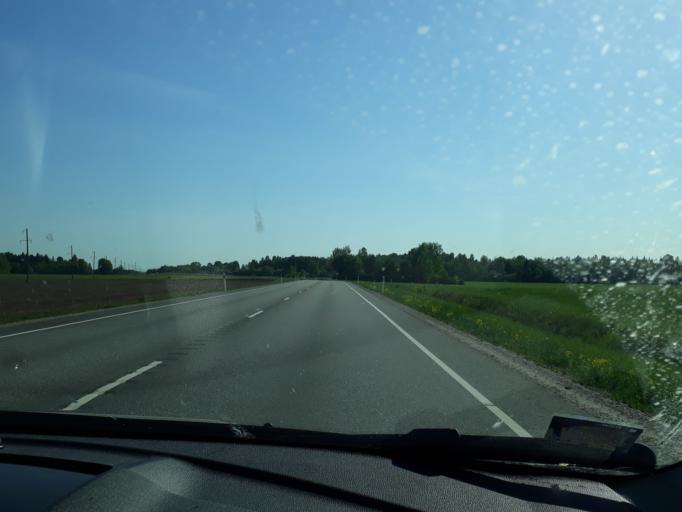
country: EE
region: Paernumaa
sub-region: Tootsi vald
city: Tootsi
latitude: 58.5744
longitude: 24.8815
